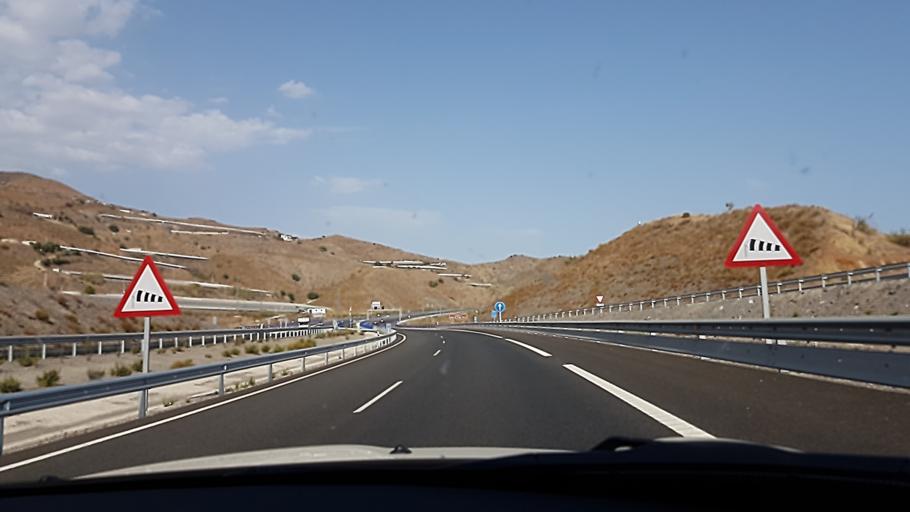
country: ES
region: Andalusia
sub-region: Provincia de Granada
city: Polopos
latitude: 36.7489
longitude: -3.3119
